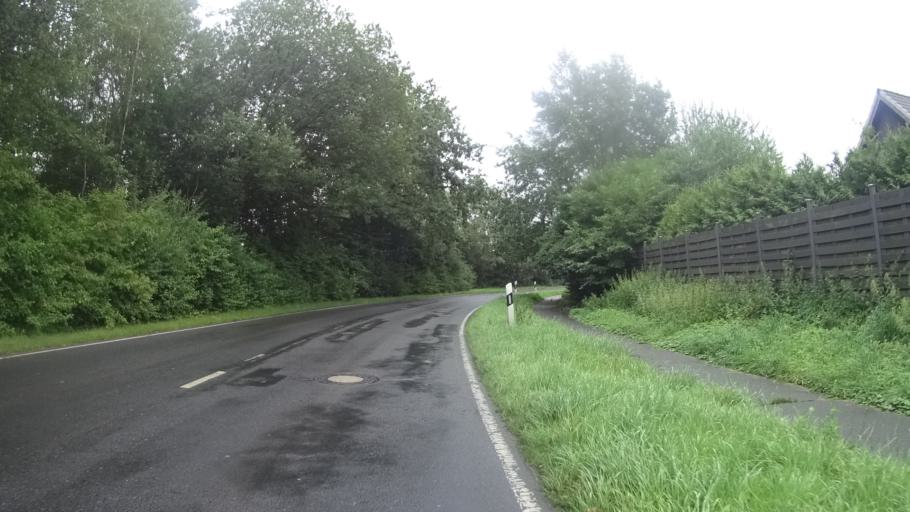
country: DE
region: Schleswig-Holstein
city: Alveslohe
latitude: 53.7885
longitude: 9.9213
